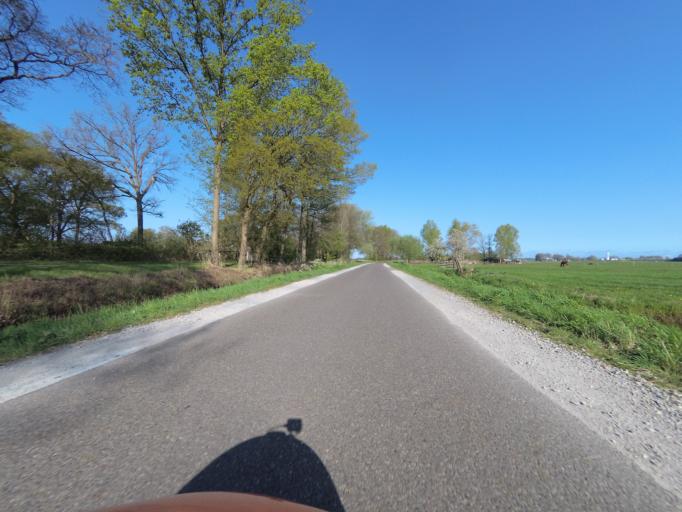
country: NL
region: North Holland
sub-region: Gemeente Naarden
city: Naarden
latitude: 52.2979
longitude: 5.1353
